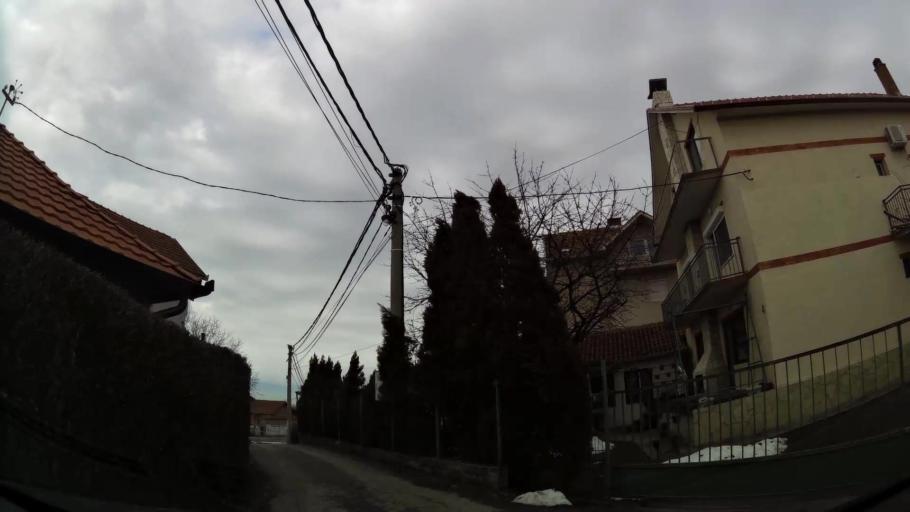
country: RS
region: Central Serbia
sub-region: Belgrade
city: Rakovica
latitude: 44.7435
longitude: 20.3958
